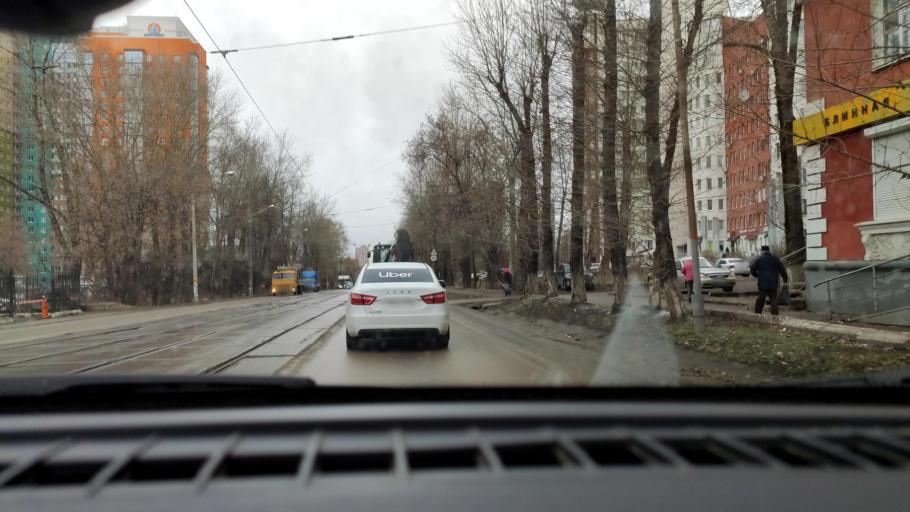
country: RU
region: Perm
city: Perm
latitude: 57.9871
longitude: 56.2174
